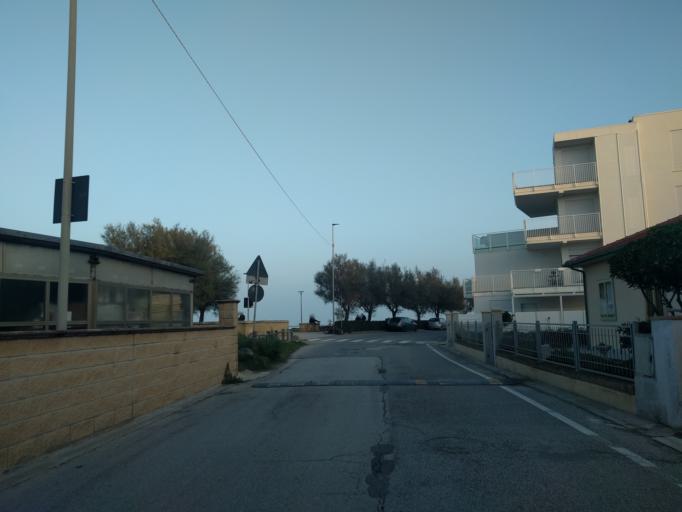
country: IT
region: The Marches
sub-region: Provincia di Ancona
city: Senigallia
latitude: 43.7421
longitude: 13.1838
